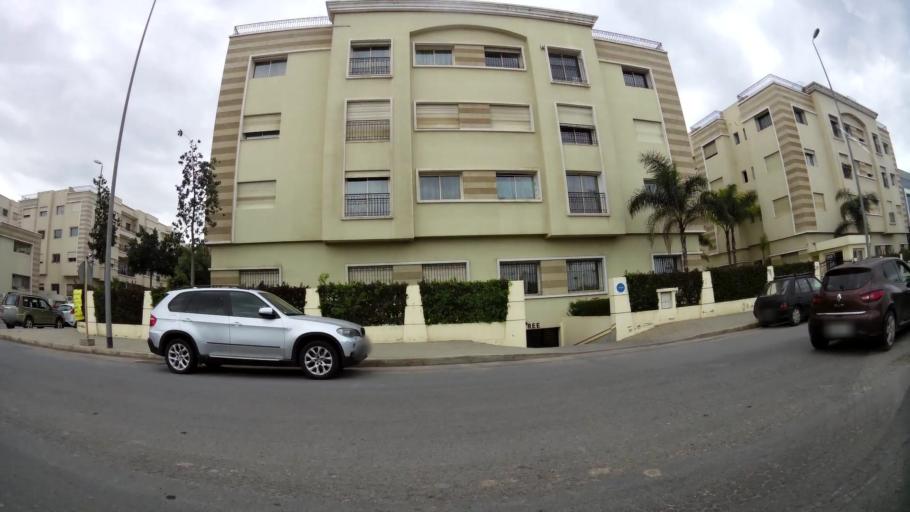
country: MA
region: Grand Casablanca
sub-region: Casablanca
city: Casablanca
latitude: 33.5489
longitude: -7.6386
